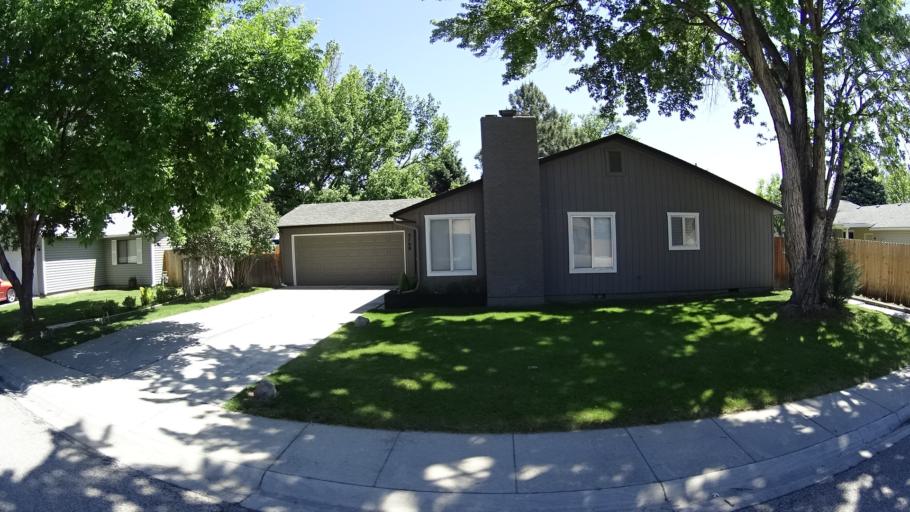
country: US
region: Idaho
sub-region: Ada County
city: Boise
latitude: 43.5681
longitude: -116.1689
